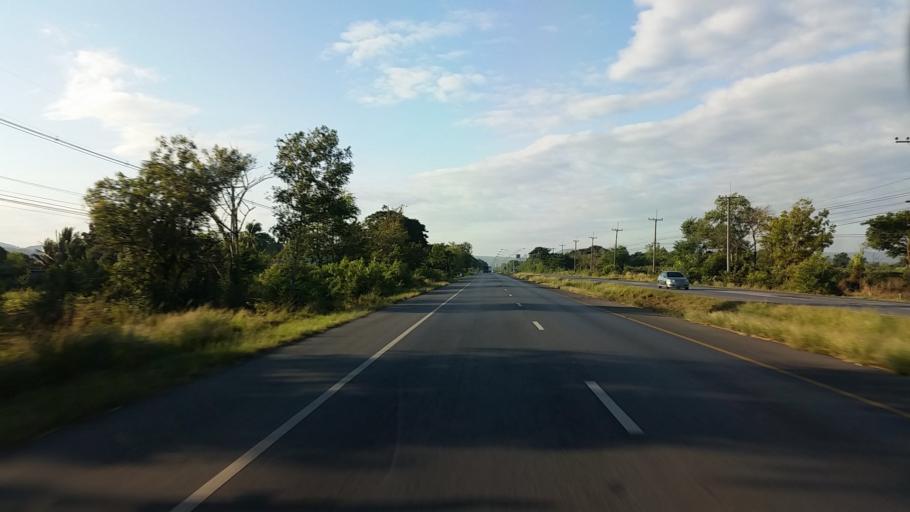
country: TH
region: Lop Buri
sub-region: Amphoe Tha Luang
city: Tha Luang
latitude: 15.0244
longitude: 100.9489
